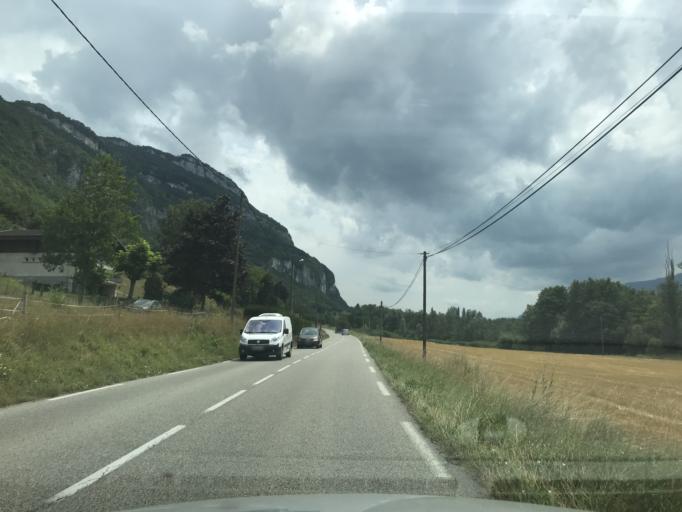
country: FR
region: Rhone-Alpes
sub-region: Departement de la Savoie
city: Chatillon
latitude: 45.8053
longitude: 5.8544
